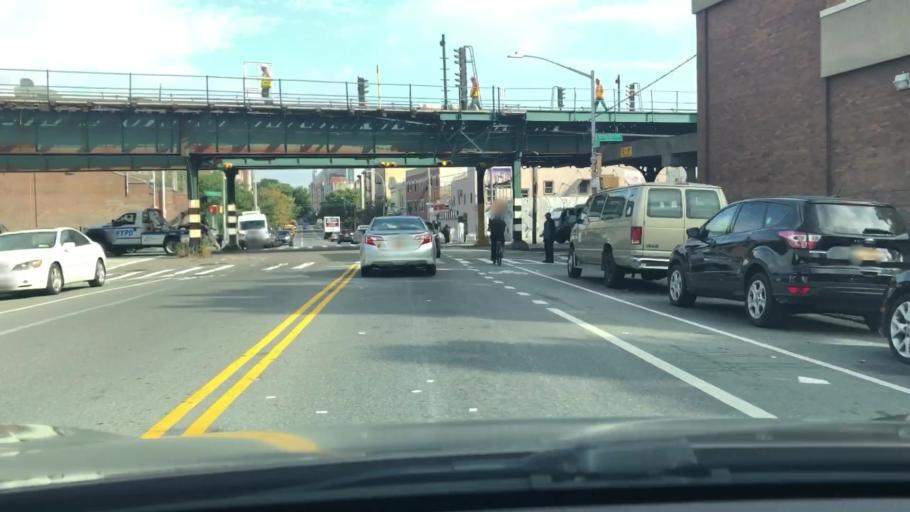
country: US
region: New York
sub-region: New York County
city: Inwood
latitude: 40.8157
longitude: -73.9121
